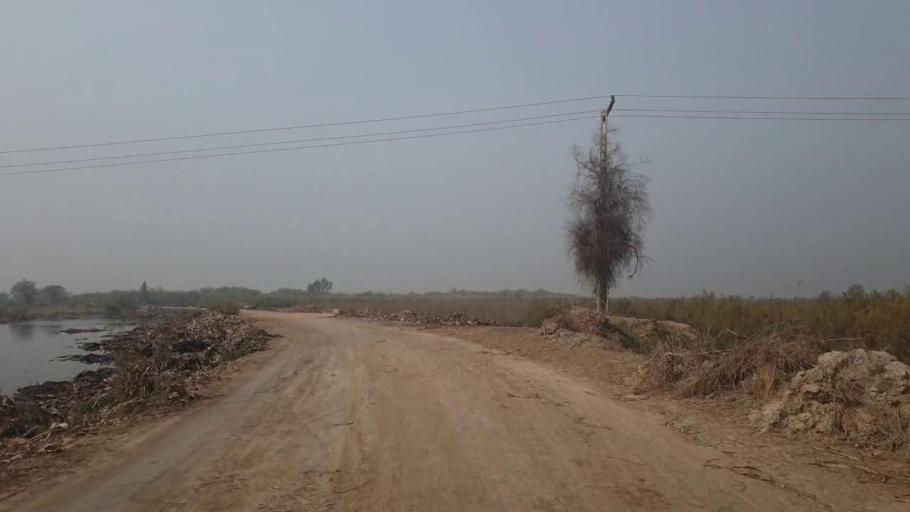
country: PK
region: Sindh
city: Tando Adam
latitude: 25.7735
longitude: 68.5745
